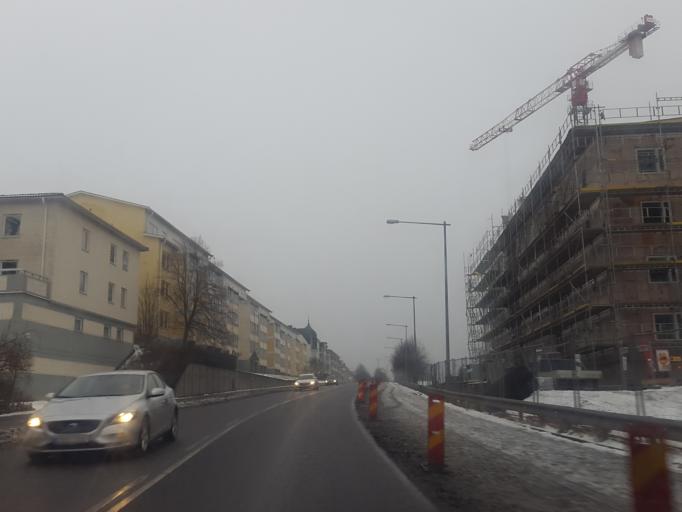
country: SE
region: Joenkoeping
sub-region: Jonkopings Kommun
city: Jonkoping
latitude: 57.7686
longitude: 14.1541
